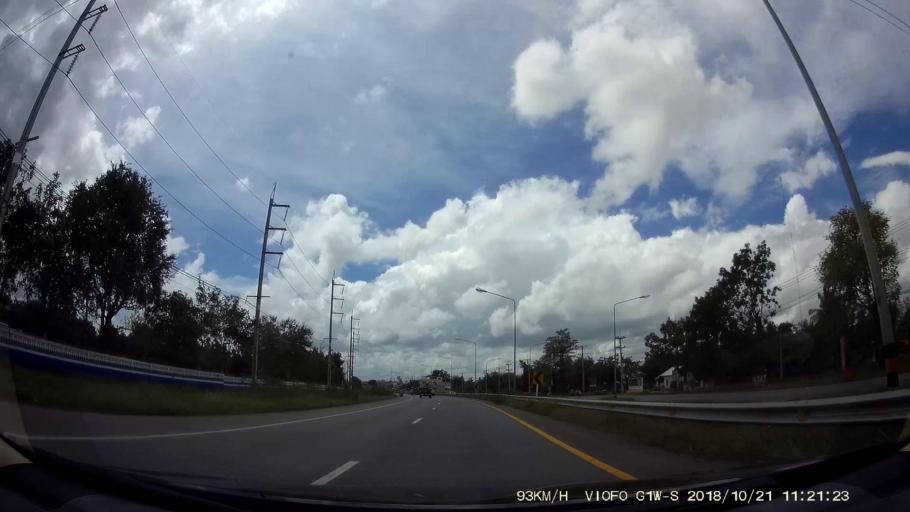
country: TH
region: Chaiyaphum
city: Chaiyaphum
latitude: 15.8472
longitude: 102.0656
